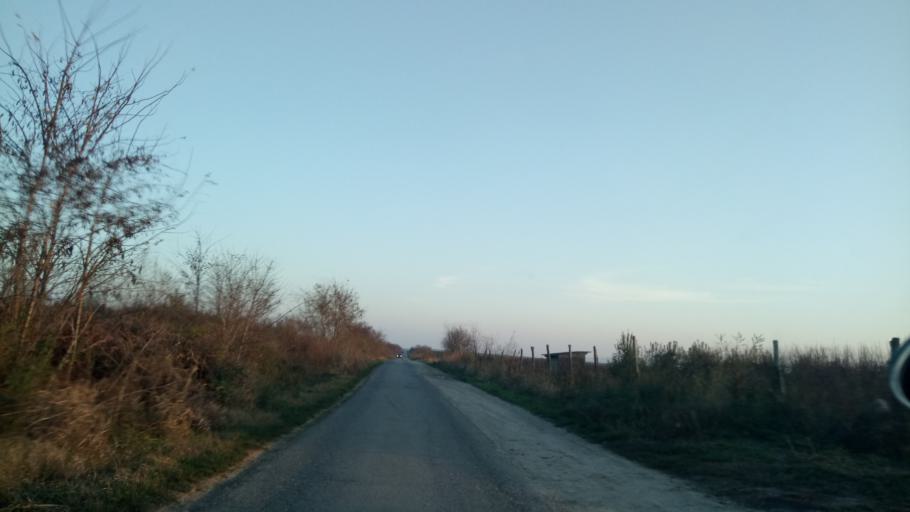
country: RS
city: Novi Slankamen
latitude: 45.1151
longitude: 20.2729
